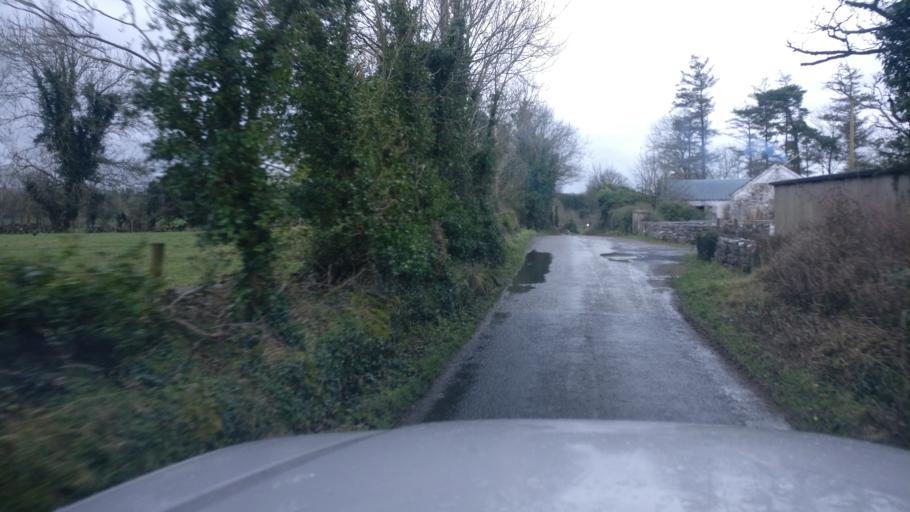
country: IE
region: Connaught
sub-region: County Galway
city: Athenry
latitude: 53.1888
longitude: -8.6927
